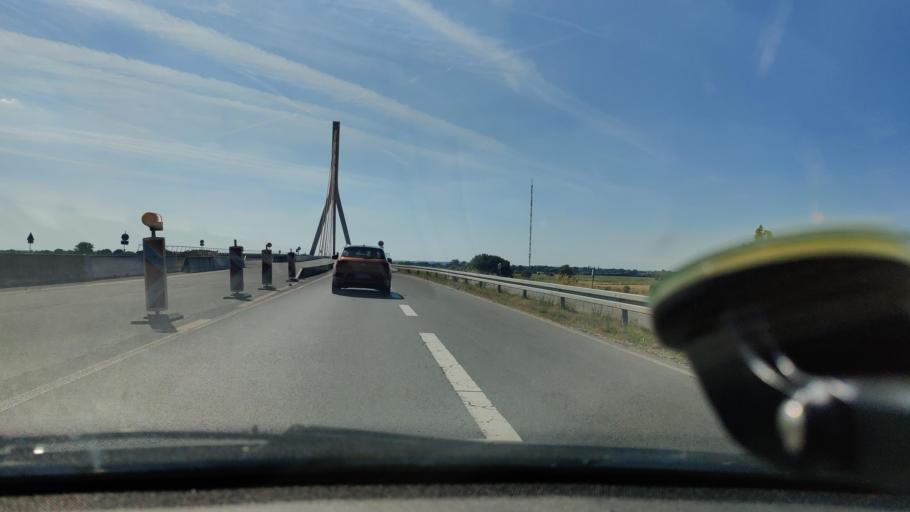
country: DE
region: North Rhine-Westphalia
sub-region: Regierungsbezirk Dusseldorf
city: Wesel
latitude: 51.6455
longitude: 6.6112
